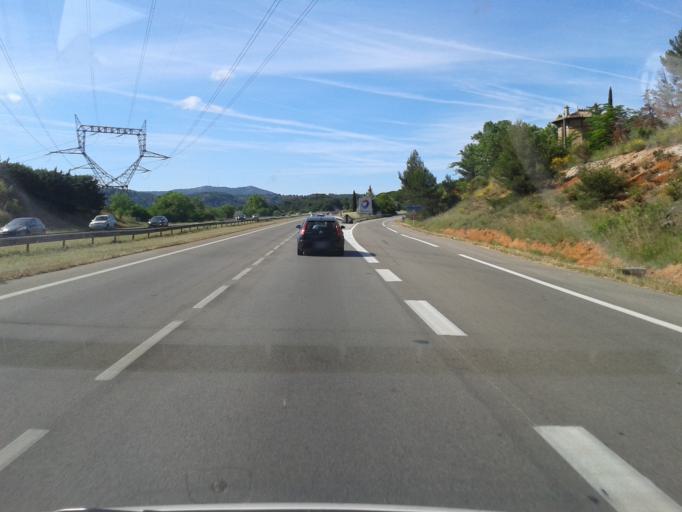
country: FR
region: Provence-Alpes-Cote d'Azur
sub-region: Departement des Bouches-du-Rhone
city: Cabries
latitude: 43.4440
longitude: 5.3959
